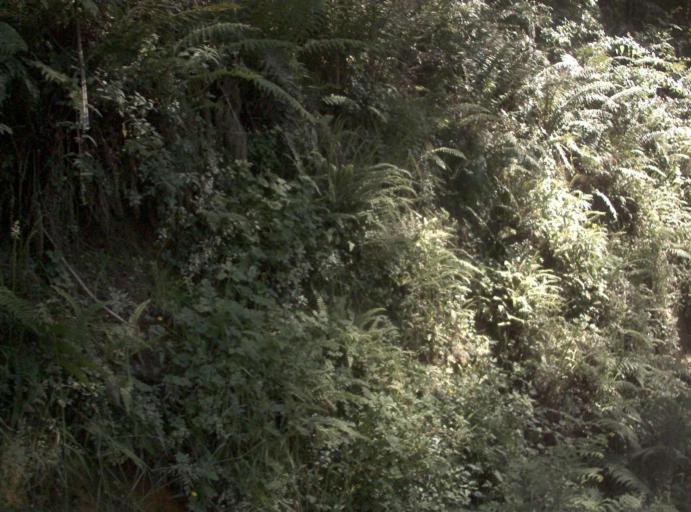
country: AU
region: Victoria
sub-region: Yarra Ranges
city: Millgrove
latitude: -37.7152
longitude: 145.6308
